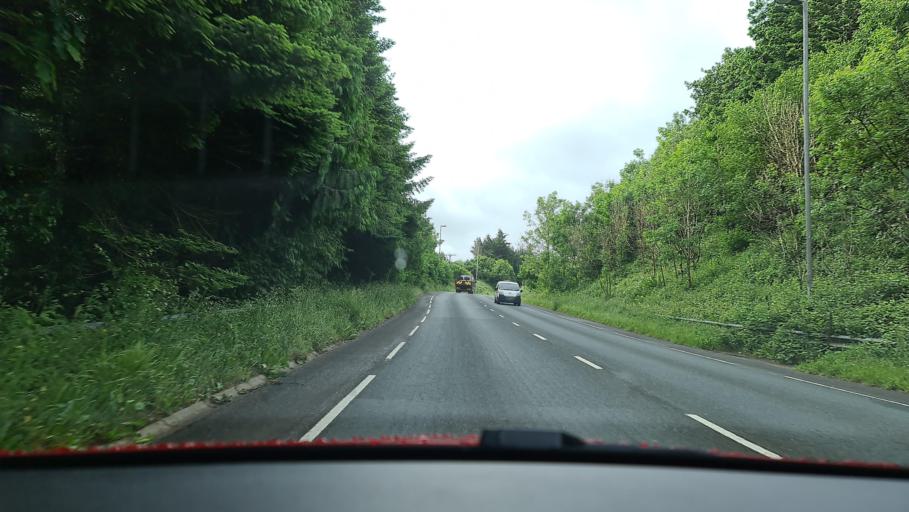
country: GB
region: England
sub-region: Cornwall
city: Liskeard
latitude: 50.4540
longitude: -4.4497
